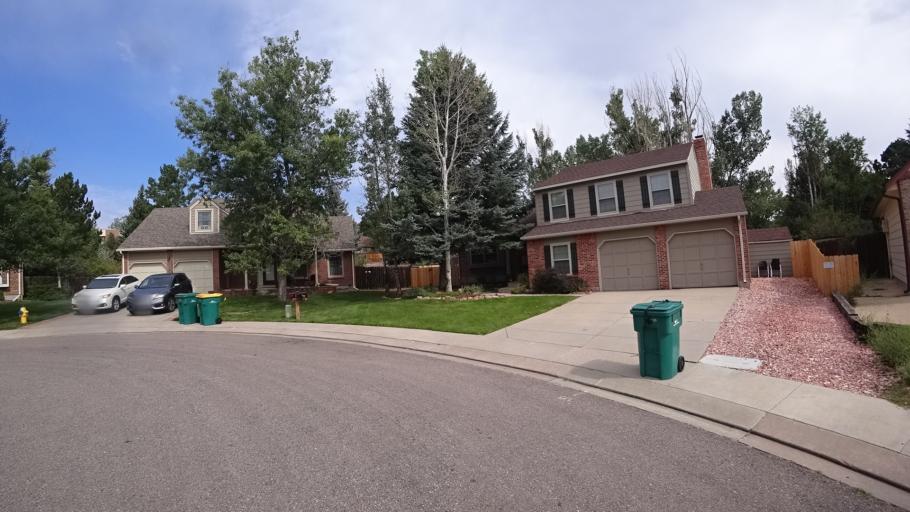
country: US
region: Colorado
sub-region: El Paso County
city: Air Force Academy
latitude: 38.9246
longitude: -104.8409
